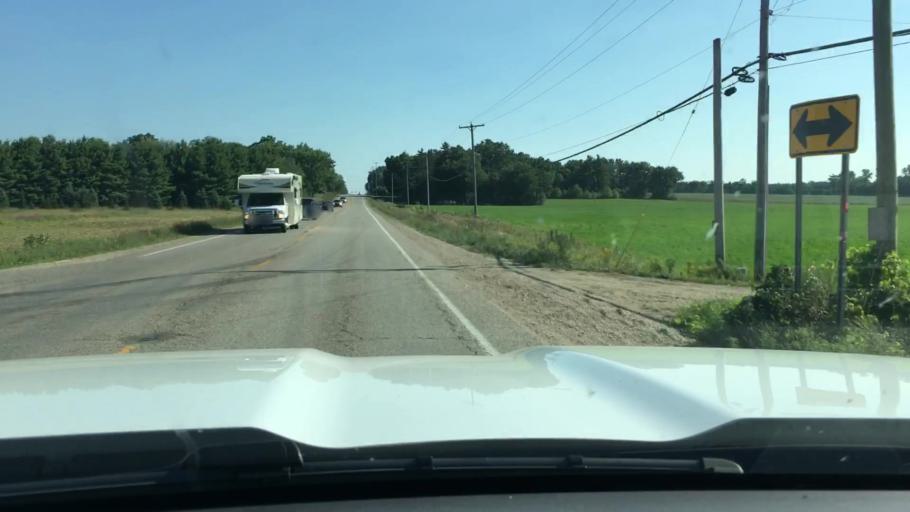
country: US
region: Michigan
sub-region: Ottawa County
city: Allendale
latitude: 43.0015
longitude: -85.9551
